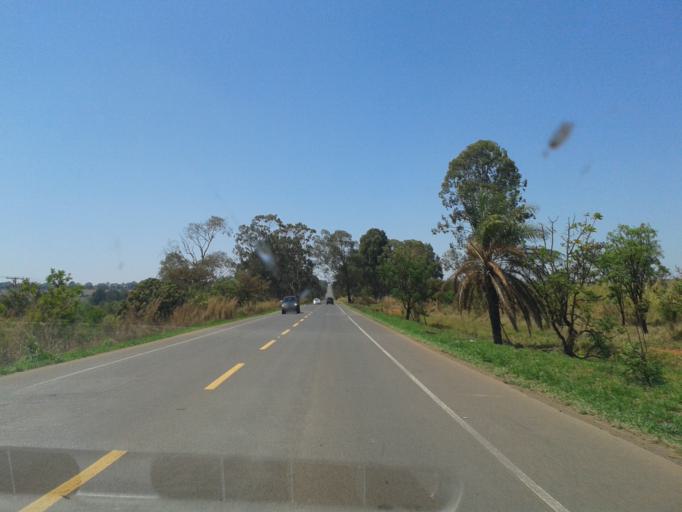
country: BR
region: Minas Gerais
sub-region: Araxa
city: Araxa
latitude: -19.3869
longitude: -47.3409
